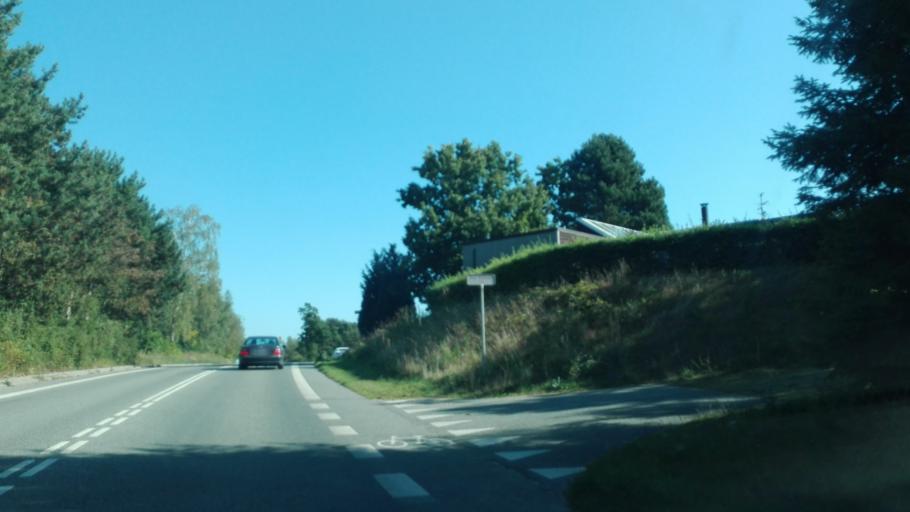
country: DK
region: Central Jutland
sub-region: Syddjurs Kommune
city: Ebeltoft
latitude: 56.2153
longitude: 10.6929
